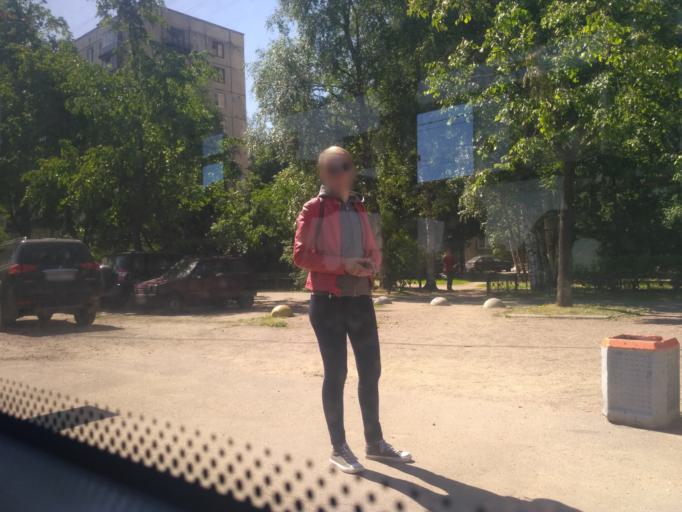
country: RU
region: Leningrad
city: Kalininskiy
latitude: 59.9642
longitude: 30.4191
